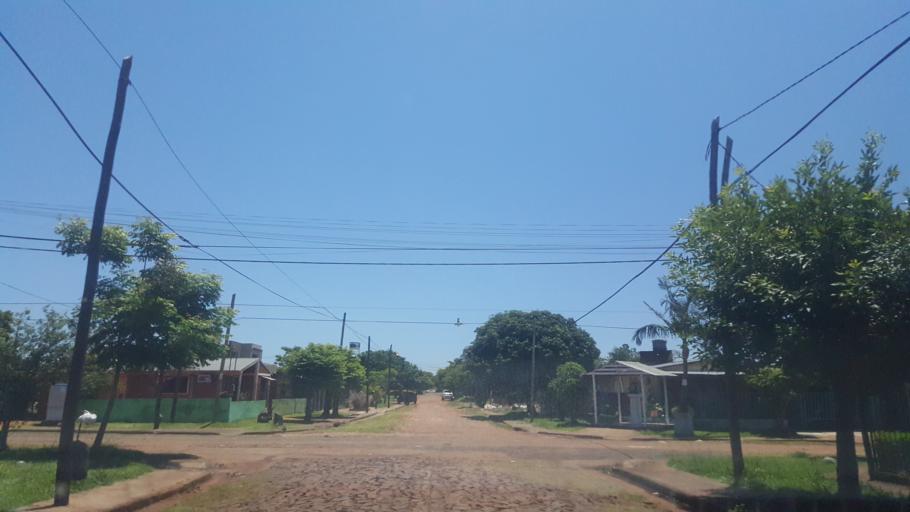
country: AR
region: Misiones
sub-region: Departamento de Capital
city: Posadas
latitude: -27.3744
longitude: -55.9154
